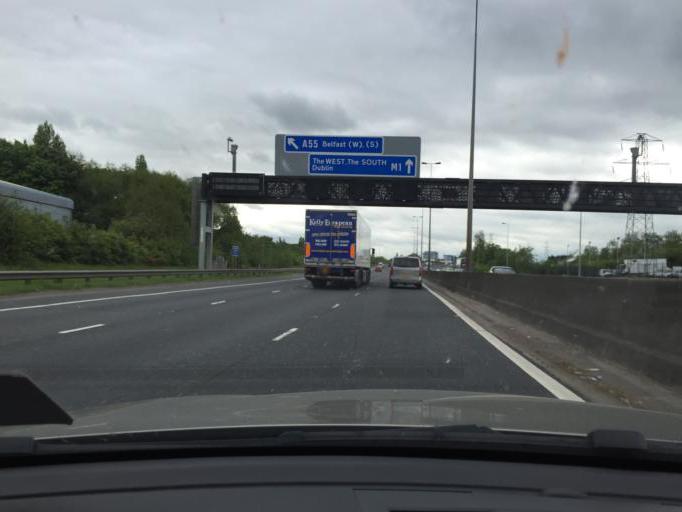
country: GB
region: Northern Ireland
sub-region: City of Belfast
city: Belfast
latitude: 54.5781
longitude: -5.9706
